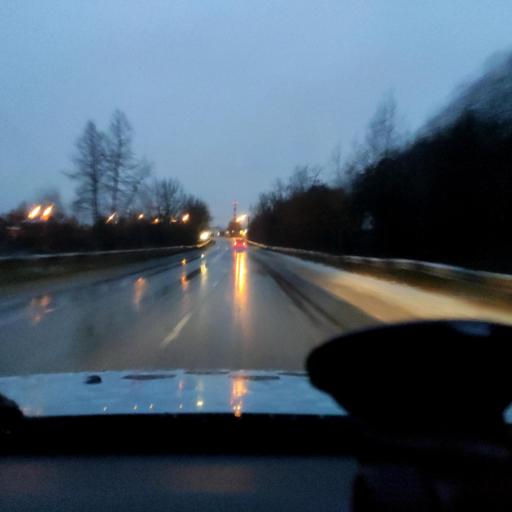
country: RU
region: Perm
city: Froly
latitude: 57.9562
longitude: 56.2942
